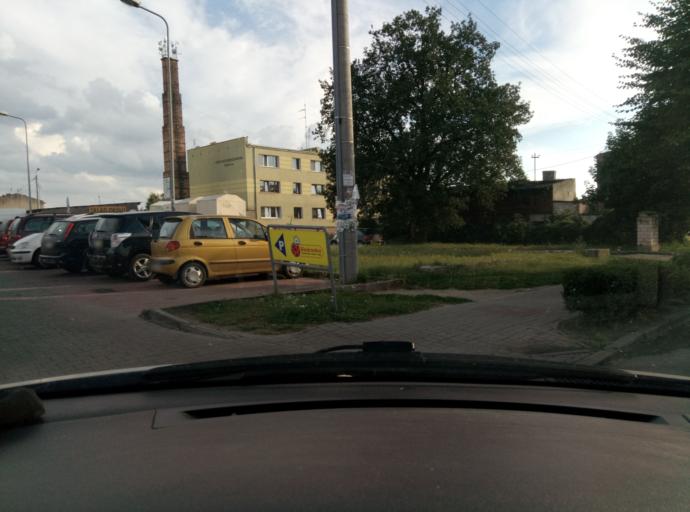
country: PL
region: Kujawsko-Pomorskie
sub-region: Powiat brodnicki
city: Jablonowo Pomorskie
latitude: 53.3917
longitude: 19.1568
